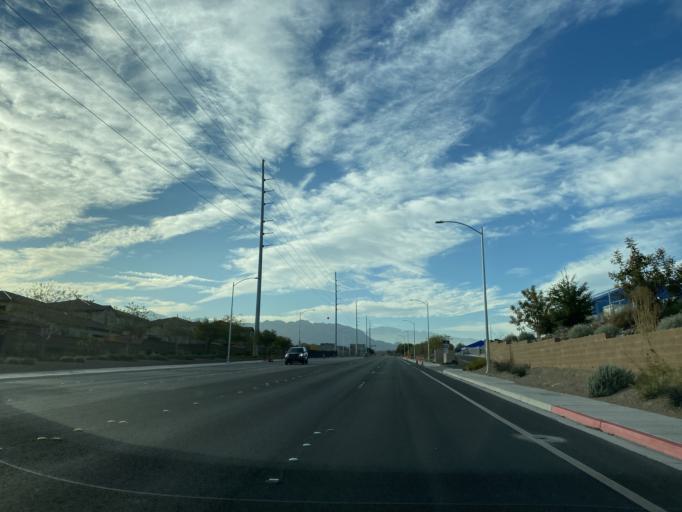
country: US
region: Nevada
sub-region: Clark County
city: Summerlin South
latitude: 36.2994
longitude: -115.3085
